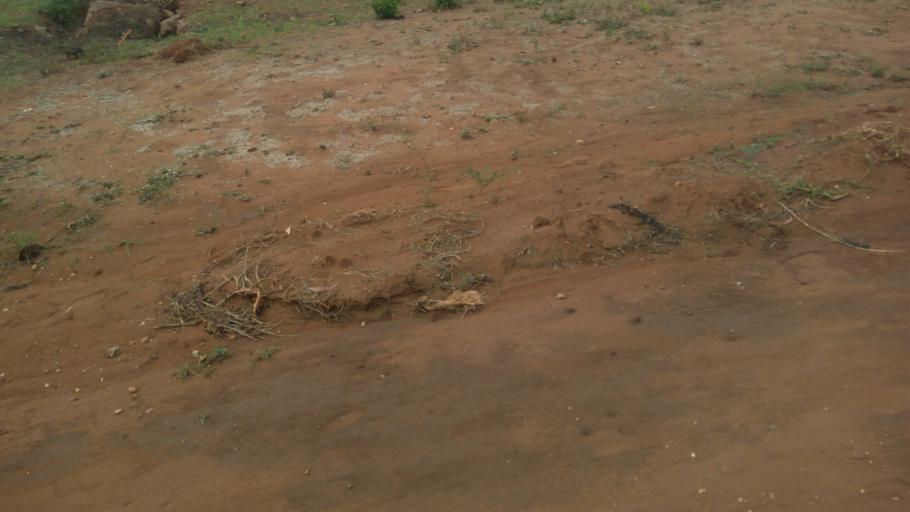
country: BJ
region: Atlantique
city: Abomey-Calavi
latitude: 6.4122
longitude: 2.3396
